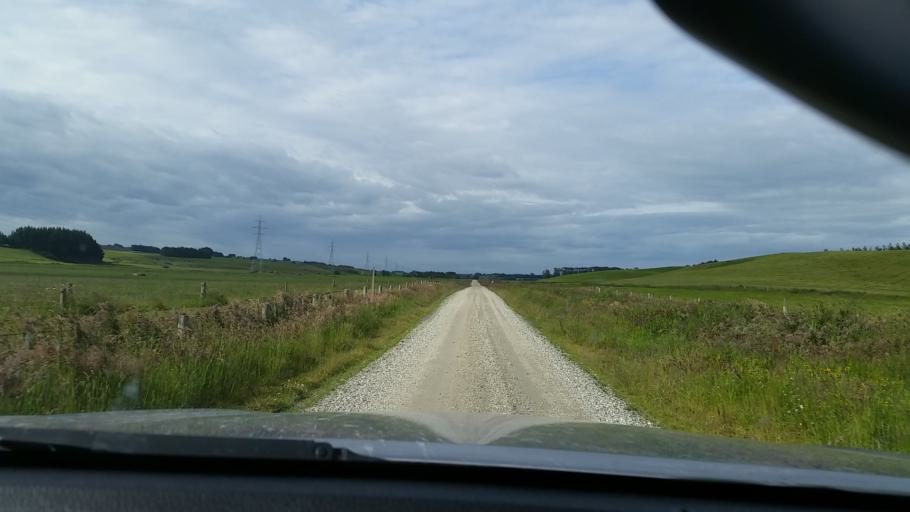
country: NZ
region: Southland
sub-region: Gore District
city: Gore
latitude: -46.2129
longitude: 168.7577
